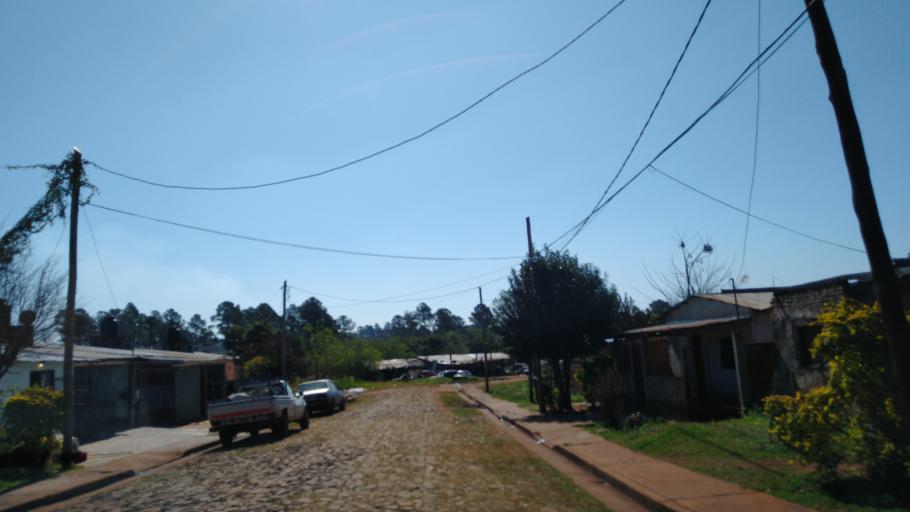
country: AR
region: Misiones
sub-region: Departamento de Capital
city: Posadas
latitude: -27.4188
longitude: -55.9616
